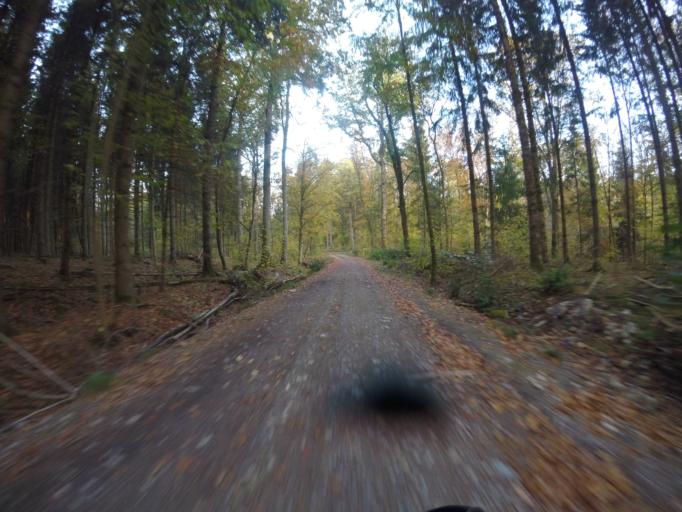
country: DE
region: Baden-Wuerttemberg
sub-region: Regierungsbezirk Stuttgart
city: Kirchberg an der Murr
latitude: 48.9816
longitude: 9.3381
